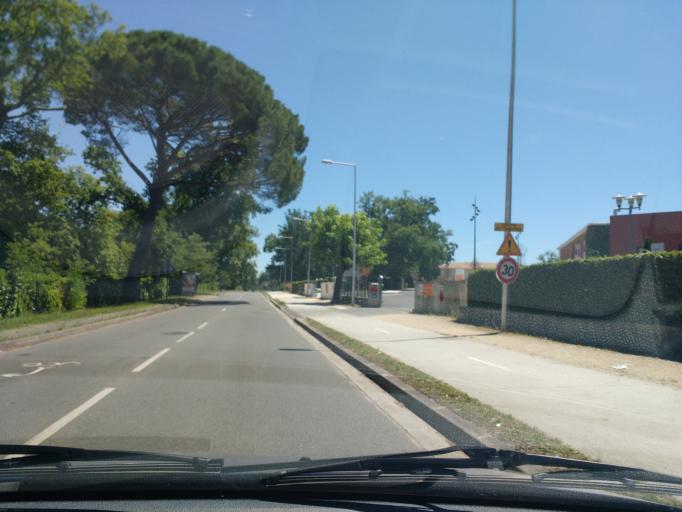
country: FR
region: Aquitaine
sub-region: Departement de la Gironde
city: Gradignan
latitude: 44.7765
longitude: -0.6052
